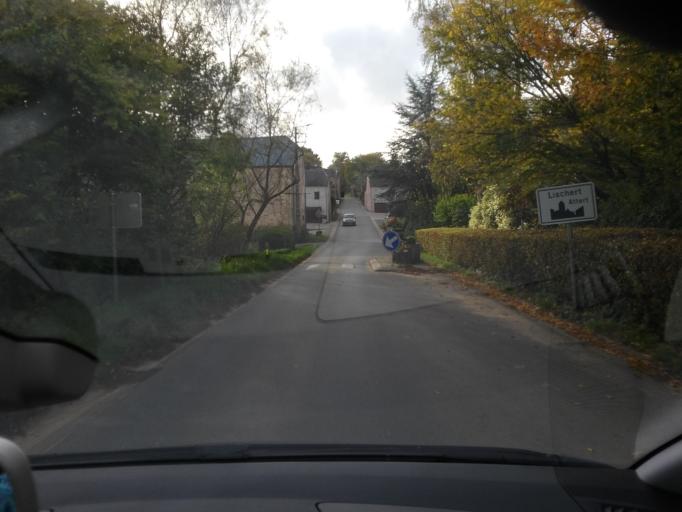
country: BE
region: Wallonia
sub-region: Province du Luxembourg
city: Attert
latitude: 49.7208
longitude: 5.7595
